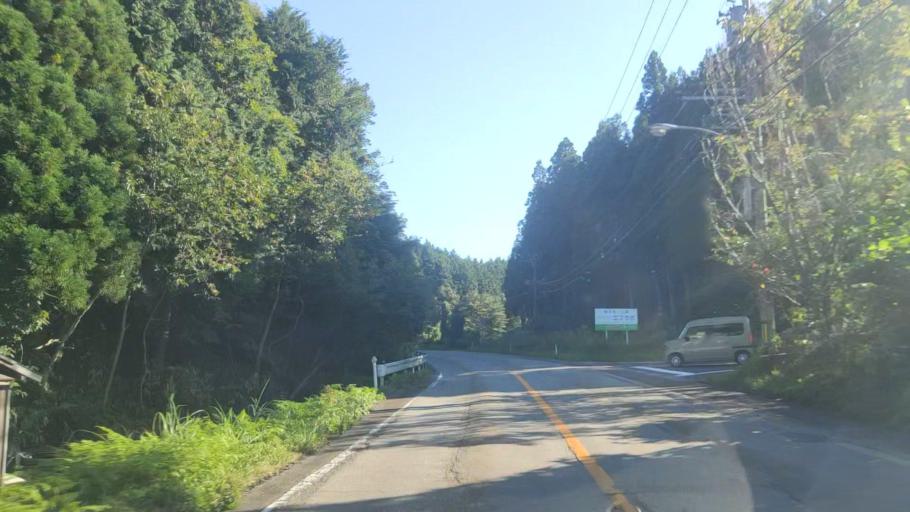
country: JP
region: Ishikawa
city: Nanao
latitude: 37.1345
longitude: 136.8629
